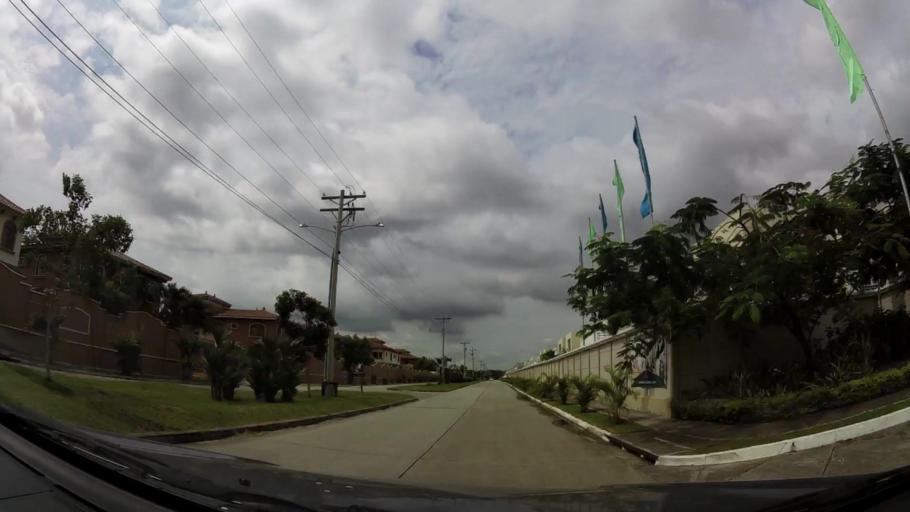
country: PA
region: Panama
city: San Miguelito
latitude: 9.0334
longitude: -79.4239
